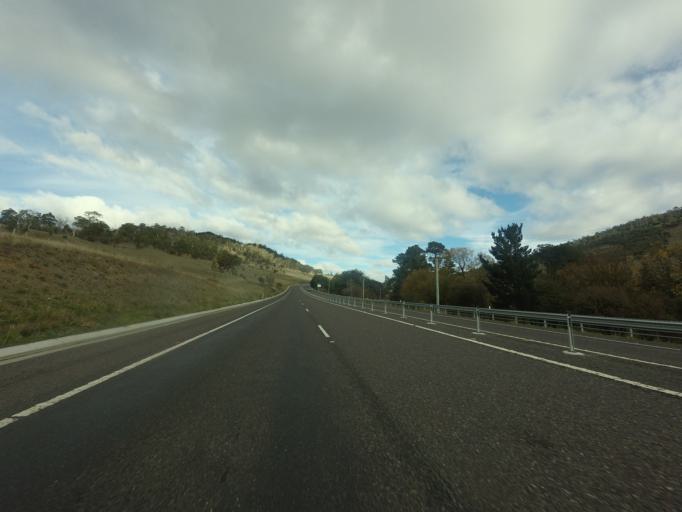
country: AU
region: Tasmania
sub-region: Brighton
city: Bridgewater
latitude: -42.5489
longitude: 147.2084
